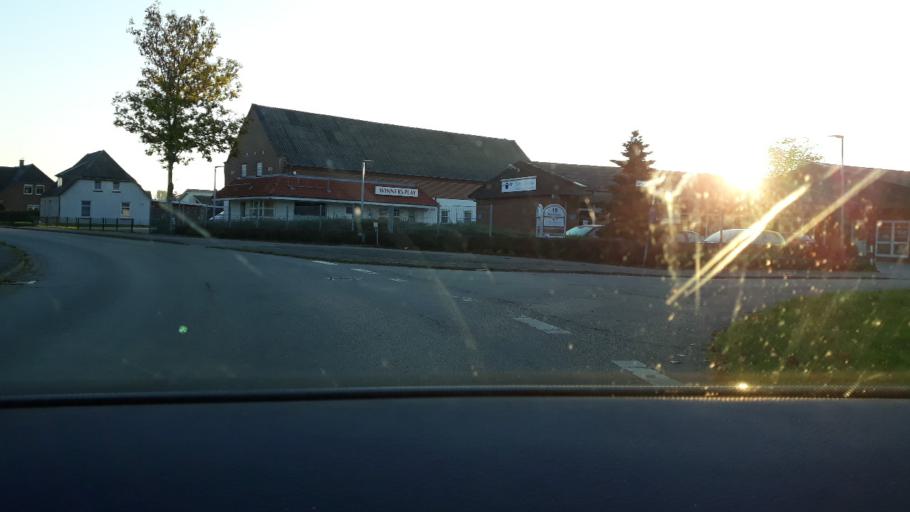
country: DE
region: Schleswig-Holstein
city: Satrup
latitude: 54.6940
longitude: 9.6056
